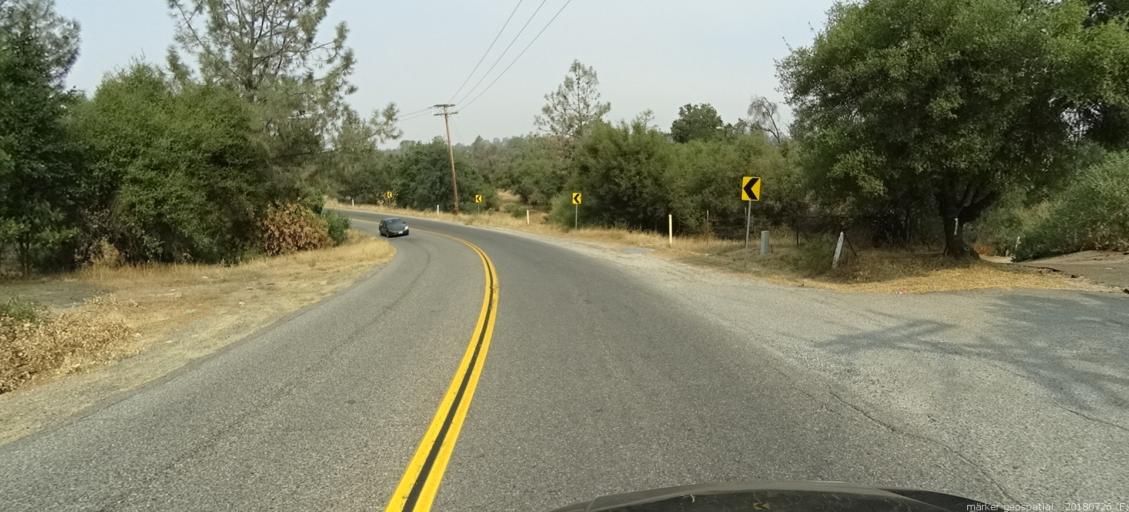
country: US
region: California
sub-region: Madera County
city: Coarsegold
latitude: 37.2194
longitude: -119.7042
